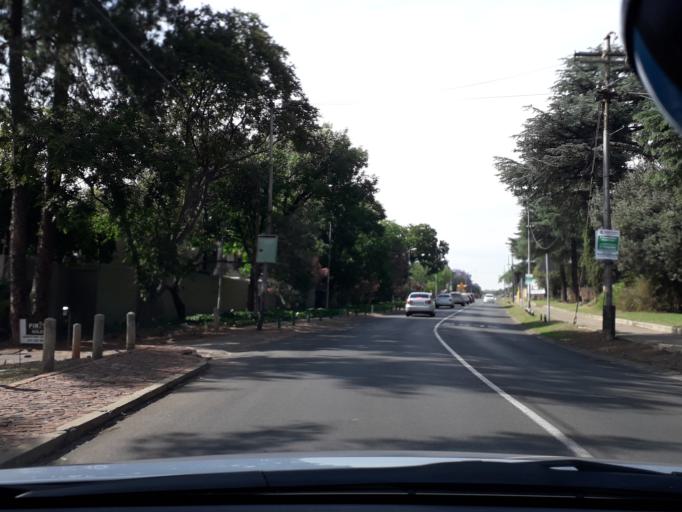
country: ZA
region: Gauteng
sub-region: City of Johannesburg Metropolitan Municipality
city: Modderfontein
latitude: -26.0771
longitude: 28.0612
